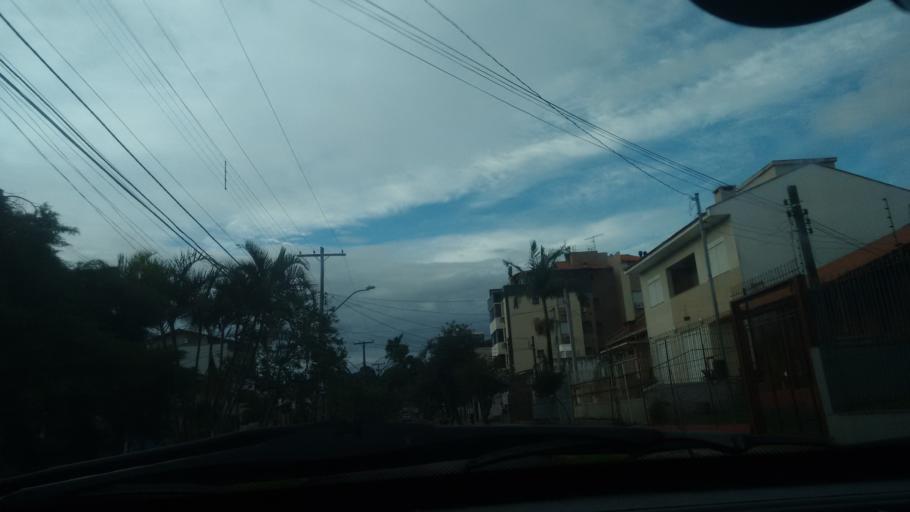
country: BR
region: Rio Grande do Sul
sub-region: Cachoeirinha
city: Cachoeirinha
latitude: -29.9998
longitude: -51.1459
